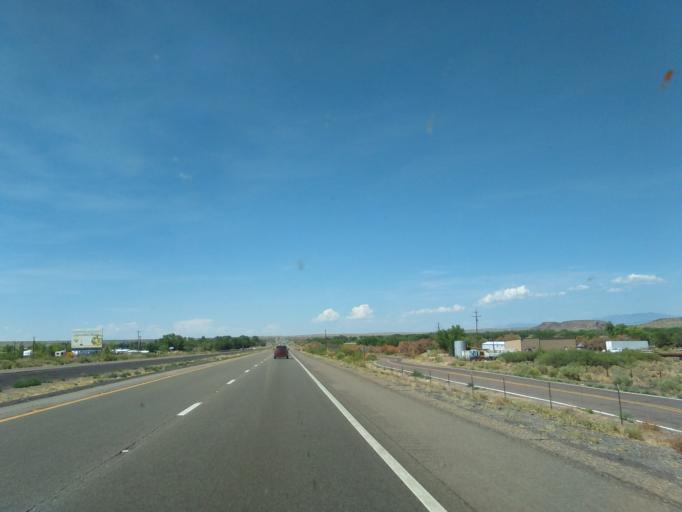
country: US
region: New Mexico
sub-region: Socorro County
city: Socorro
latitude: 34.2333
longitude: -106.9161
